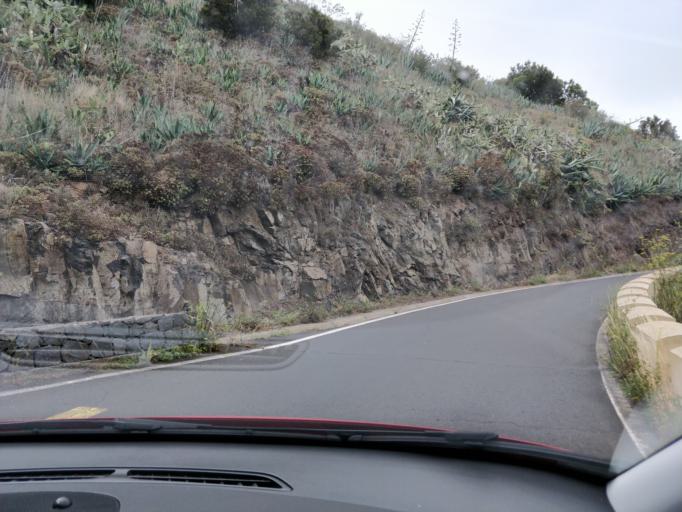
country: ES
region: Canary Islands
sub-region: Provincia de Santa Cruz de Tenerife
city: Tanque
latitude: 28.3247
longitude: -16.8529
